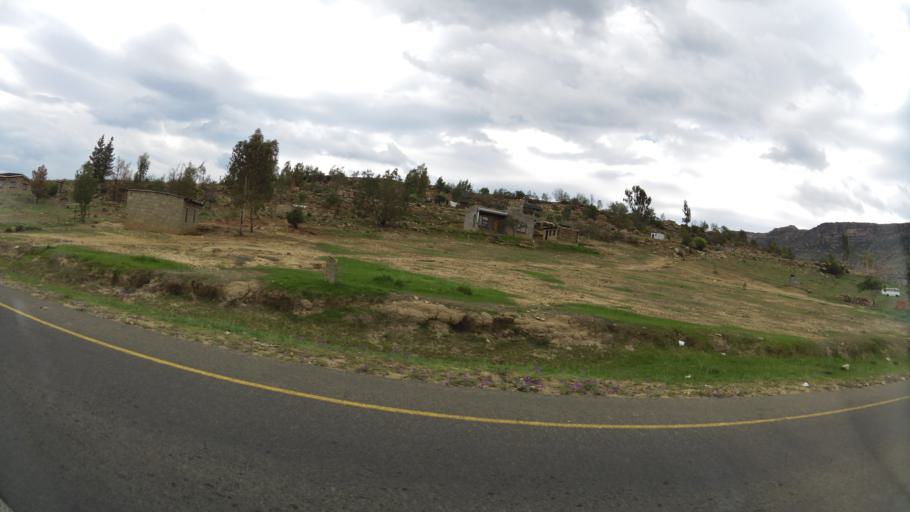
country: LS
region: Maseru
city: Maseru
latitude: -29.4031
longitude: 27.4726
